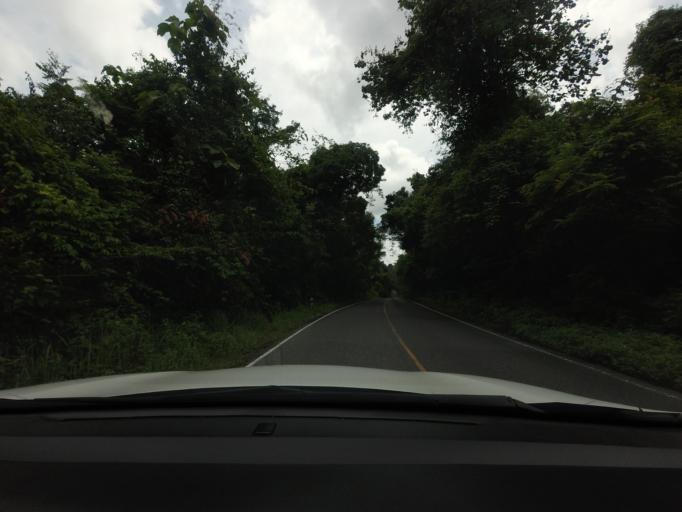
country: TH
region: Nakhon Nayok
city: Pak Phli
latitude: 14.2767
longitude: 101.3840
